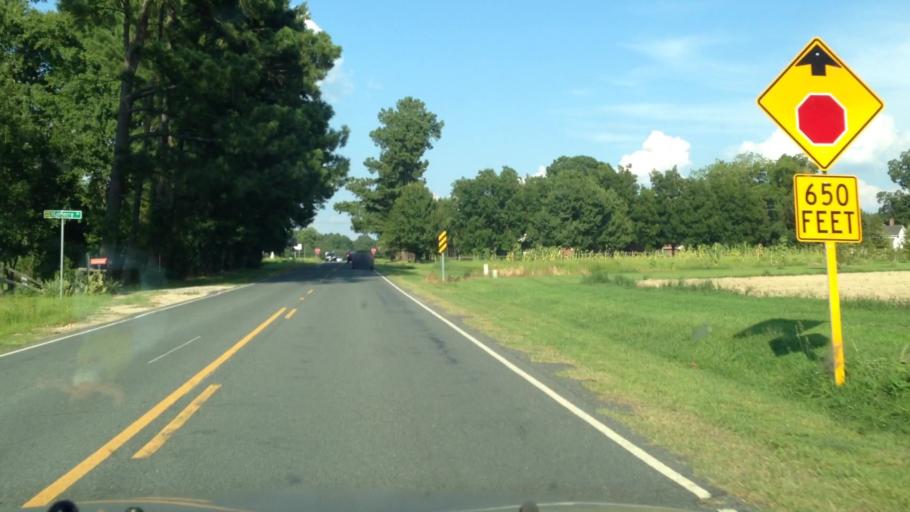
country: US
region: North Carolina
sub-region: Harnett County
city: Buies Creek
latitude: 35.4135
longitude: -78.7164
